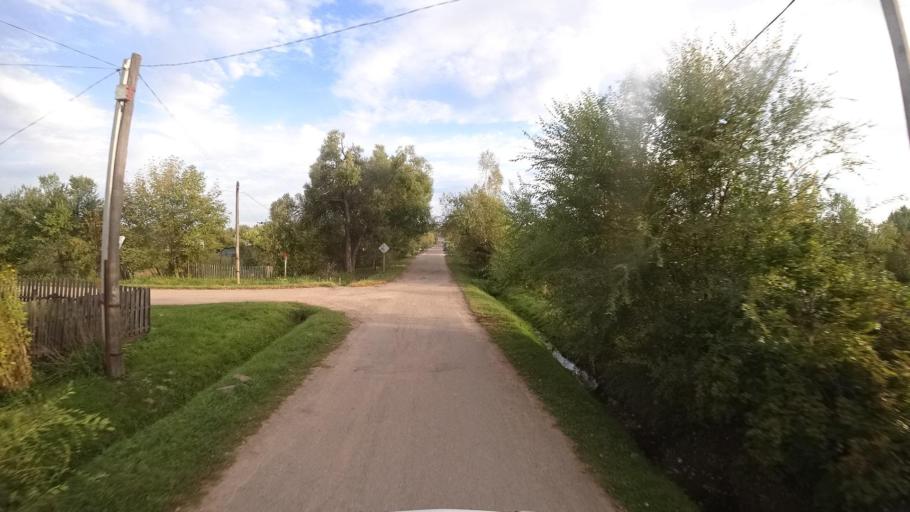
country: RU
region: Primorskiy
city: Yakovlevka
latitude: 44.4307
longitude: 133.4748
